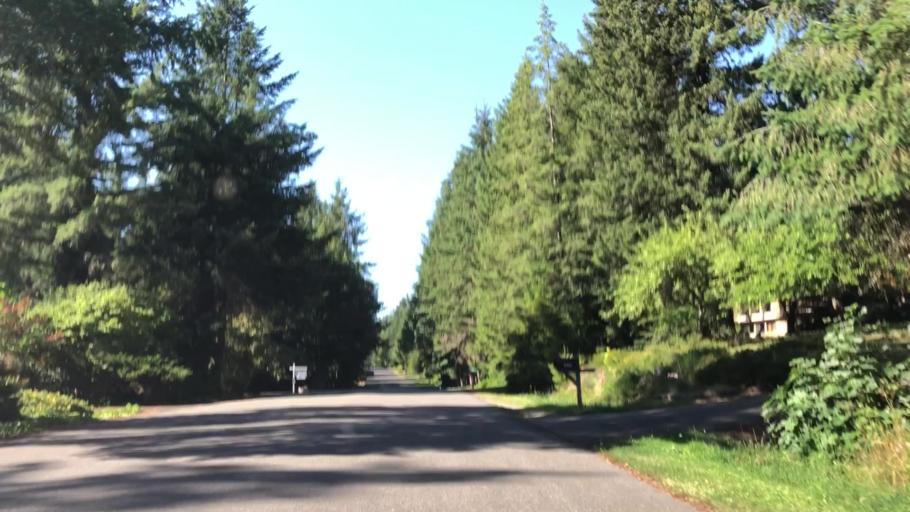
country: US
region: Washington
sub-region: King County
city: Cottage Lake
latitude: 47.7607
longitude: -122.0861
